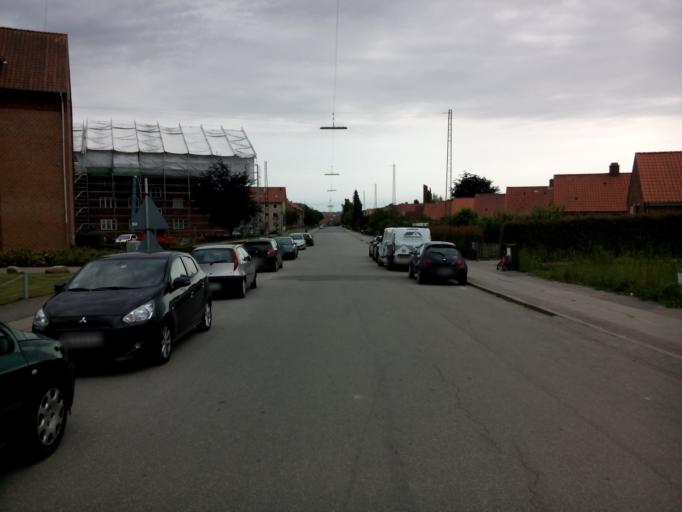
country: DK
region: Central Jutland
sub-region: Arhus Kommune
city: Arhus
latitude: 56.1691
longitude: 10.1843
